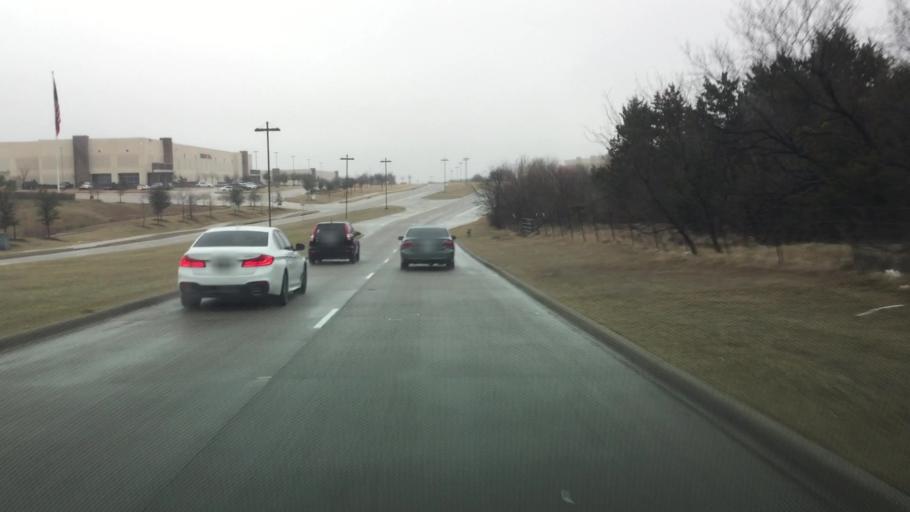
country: US
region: Texas
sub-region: Denton County
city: Flower Mound
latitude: 32.9947
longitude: -97.0590
